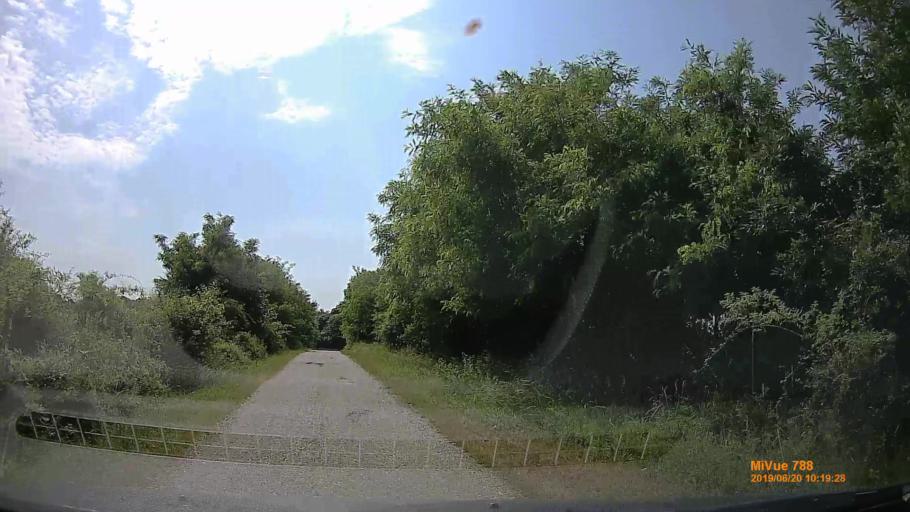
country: HU
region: Baranya
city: Mecseknadasd
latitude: 46.2112
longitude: 18.4613
